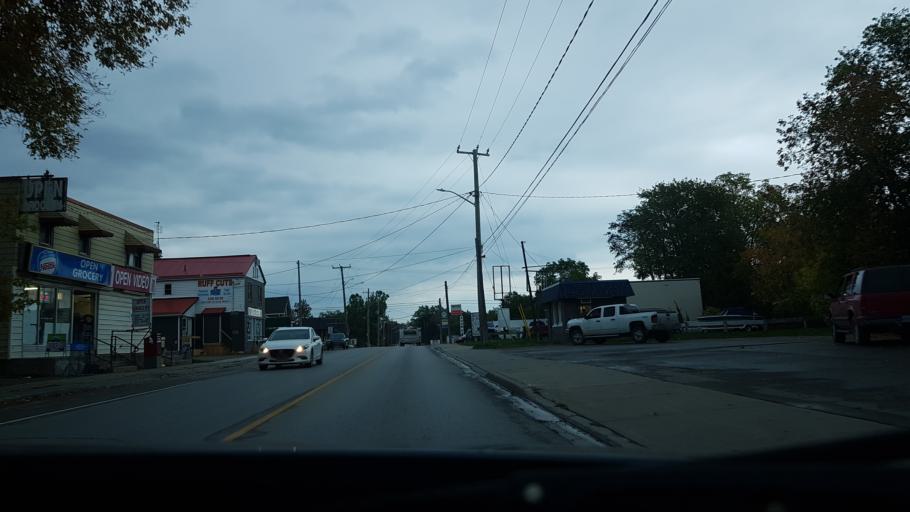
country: CA
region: Ontario
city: Omemee
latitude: 44.3597
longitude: -78.7277
